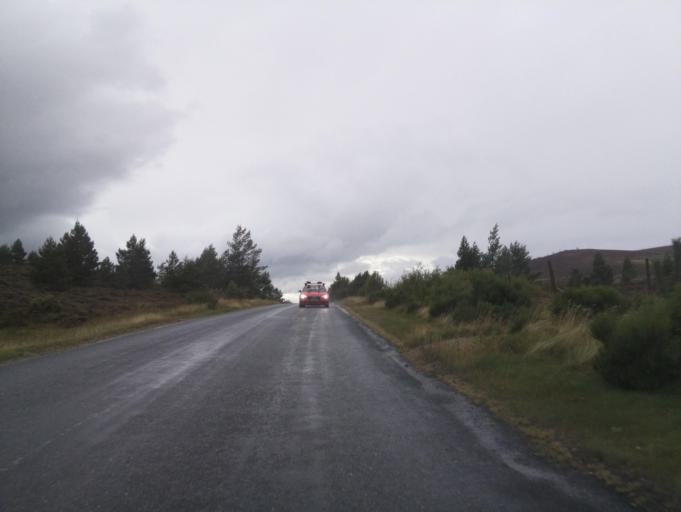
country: GB
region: Scotland
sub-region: Highland
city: Grantown on Spey
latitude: 57.2815
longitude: -3.5568
